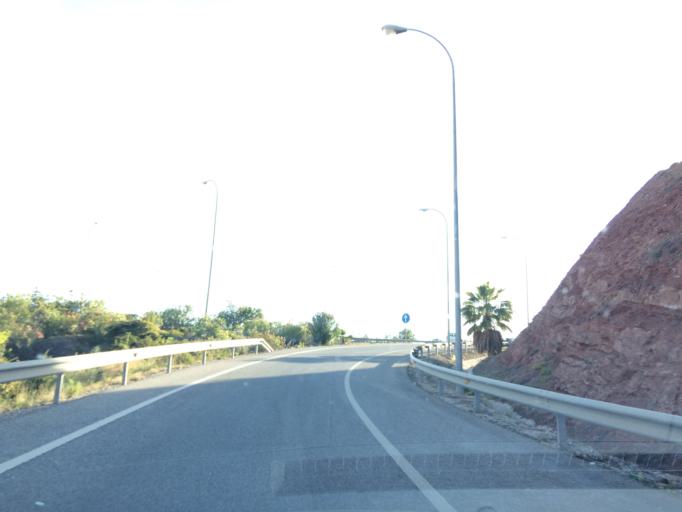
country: ES
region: Andalusia
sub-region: Provincia de Malaga
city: Totalan
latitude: 36.7246
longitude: -4.3431
